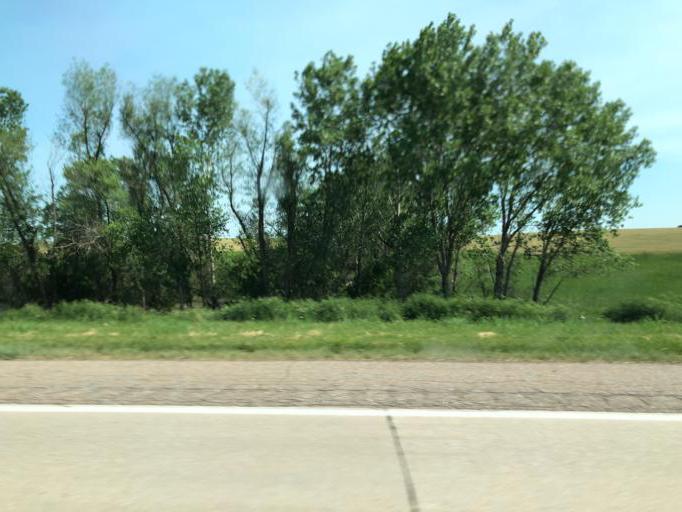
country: US
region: Nebraska
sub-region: Thayer County
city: Hebron
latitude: 40.1391
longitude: -97.5904
